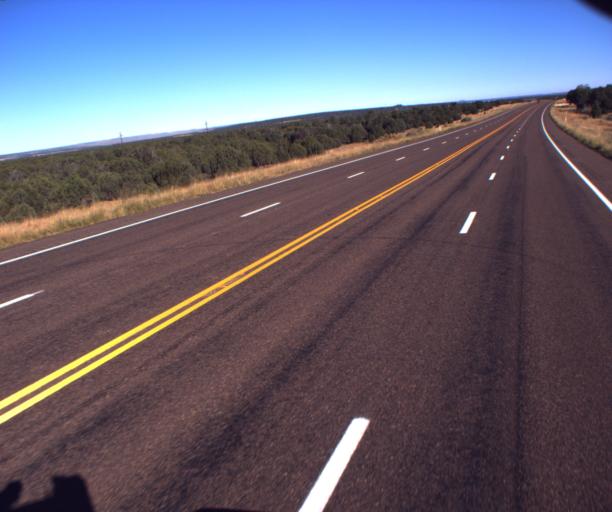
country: US
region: Arizona
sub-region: Navajo County
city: White Mountain Lake
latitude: 34.3474
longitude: -110.0527
